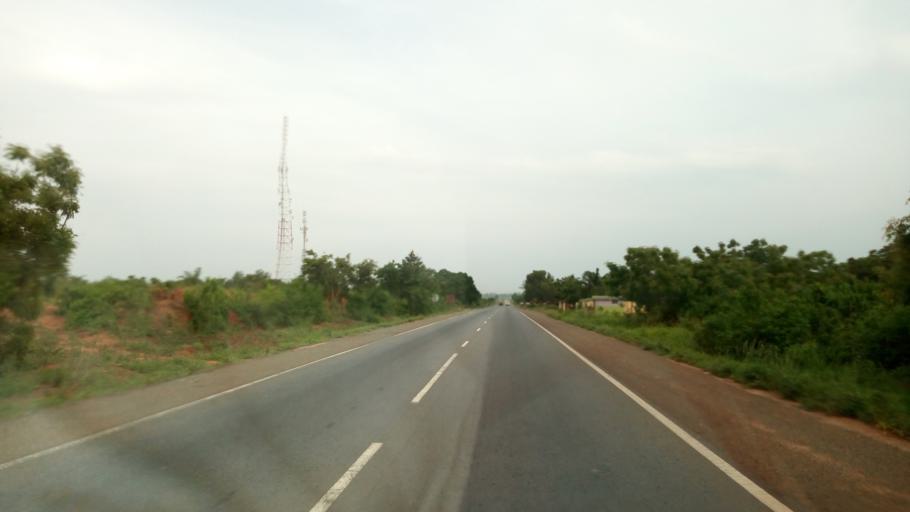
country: GH
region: Volta
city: Keta
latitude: 6.0520
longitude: 0.9692
